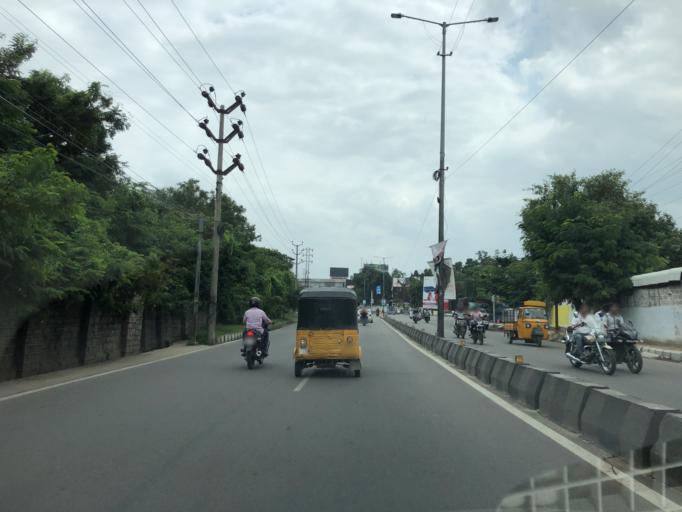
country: IN
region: Telangana
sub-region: Hyderabad
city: Malkajgiri
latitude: 17.4466
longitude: 78.4874
